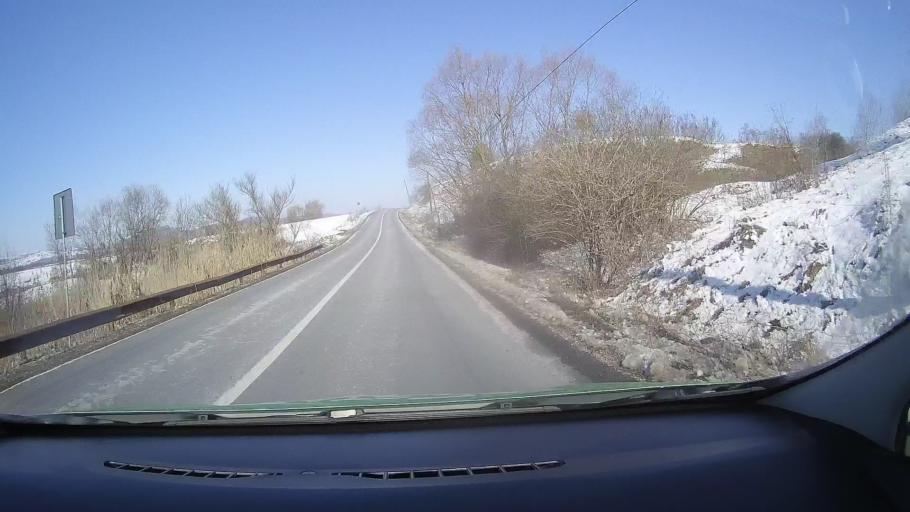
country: RO
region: Brasov
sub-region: Comuna Comana
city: Comana de Jos
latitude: 45.9010
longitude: 25.2269
